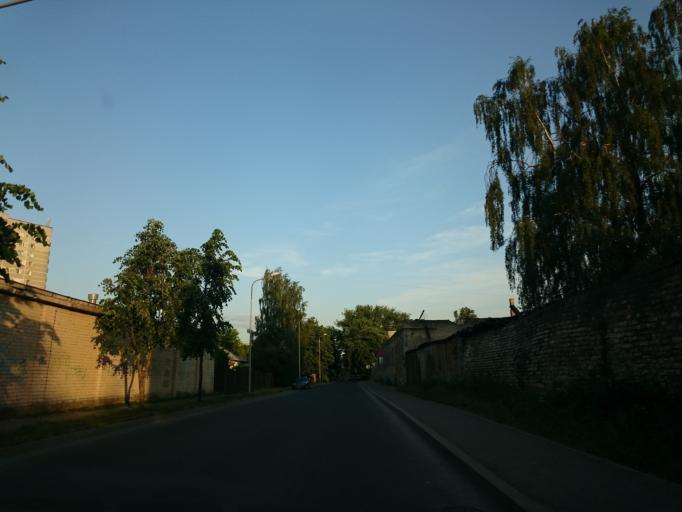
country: LV
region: Riga
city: Riga
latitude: 56.9289
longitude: 24.1673
